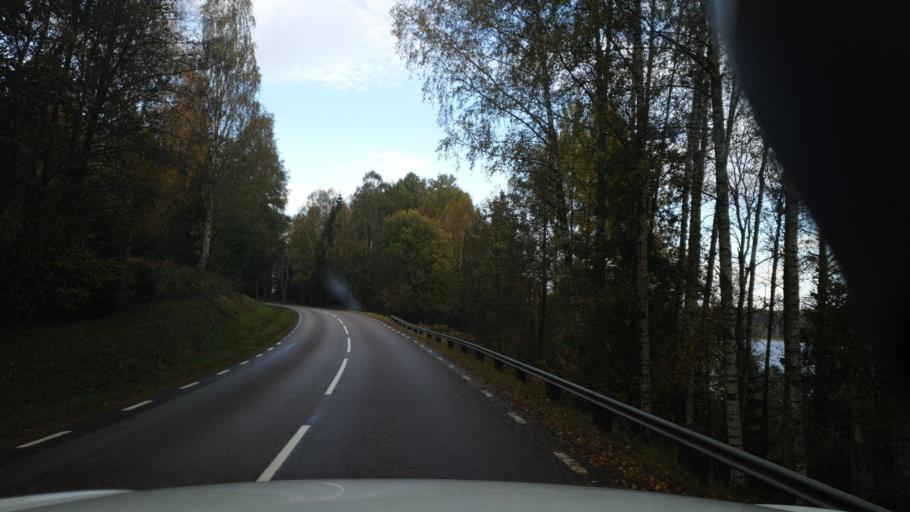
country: SE
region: Vaermland
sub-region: Arvika Kommun
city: Arvika
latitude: 59.4597
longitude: 12.7586
